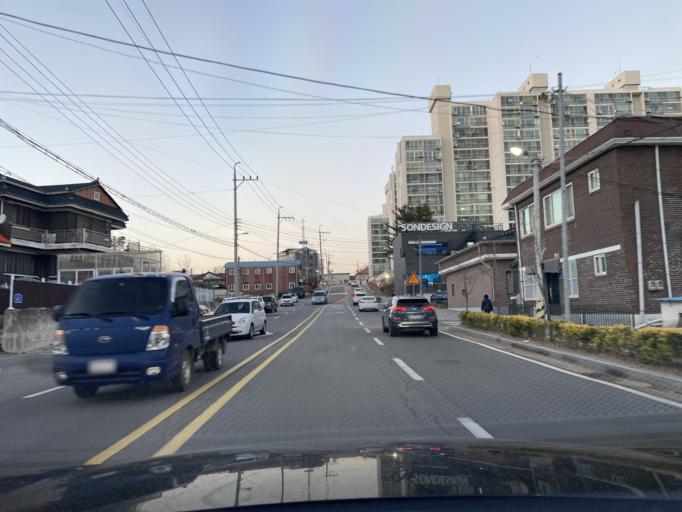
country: KR
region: Chungcheongnam-do
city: Yesan
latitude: 36.6831
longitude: 126.8436
